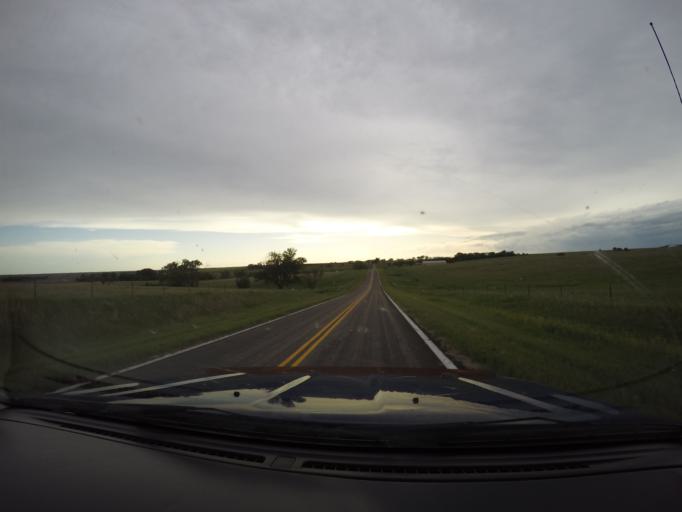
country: US
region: Kansas
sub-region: Smith County
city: Smith Center
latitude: 39.8282
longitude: -98.5704
